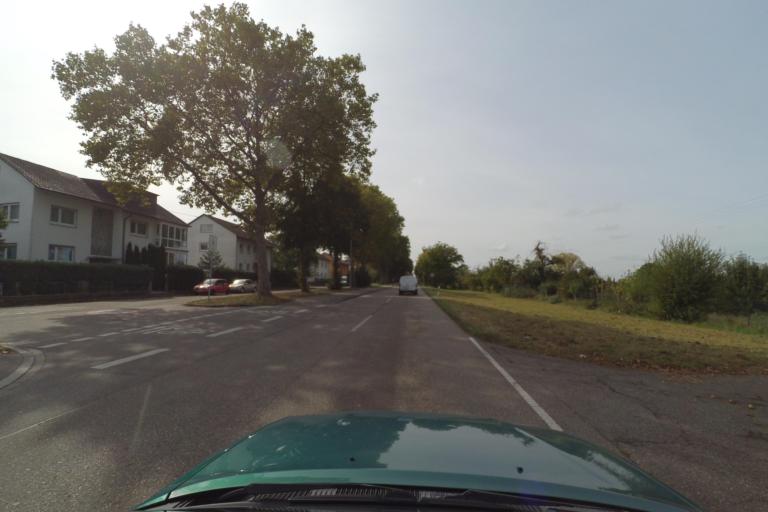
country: DE
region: Baden-Wuerttemberg
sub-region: Freiburg Region
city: Mahlberg
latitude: 48.2955
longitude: 7.8156
